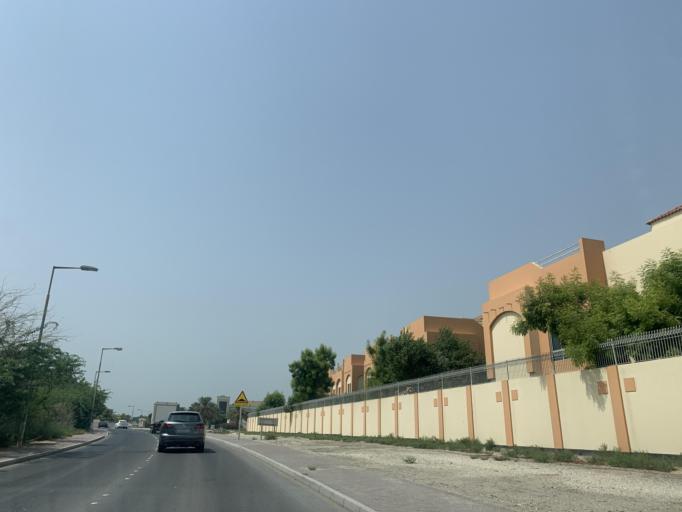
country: BH
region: Central Governorate
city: Madinat Hamad
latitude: 26.1474
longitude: 50.4561
